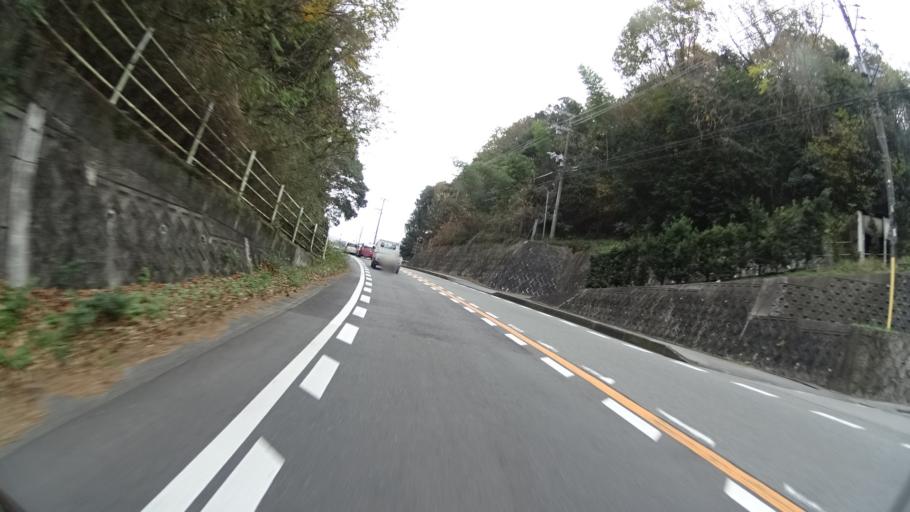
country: JP
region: Hyogo
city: Sasayama
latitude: 35.0749
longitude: 135.1655
